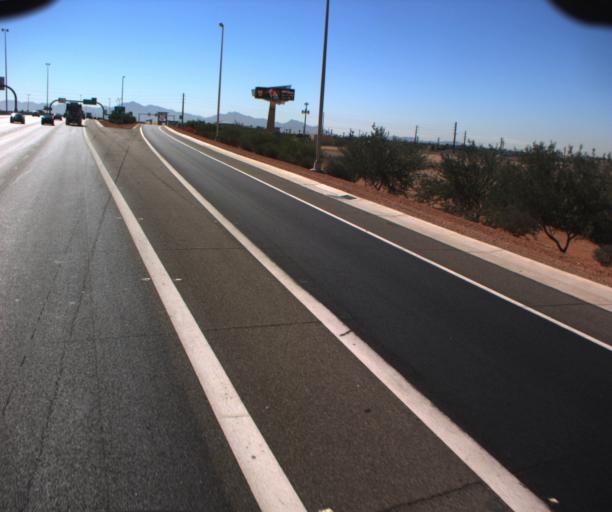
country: US
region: Arizona
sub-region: Maricopa County
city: Peoria
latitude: 33.5266
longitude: -112.2693
